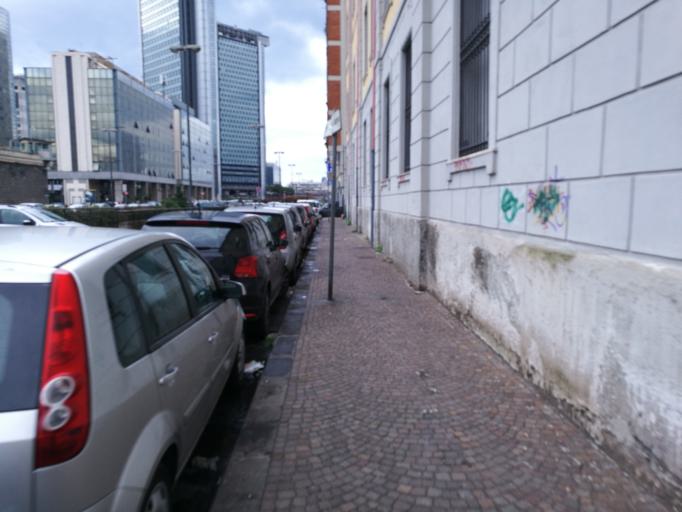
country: IT
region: Campania
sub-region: Provincia di Napoli
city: Napoli
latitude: 40.8589
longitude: 14.2769
